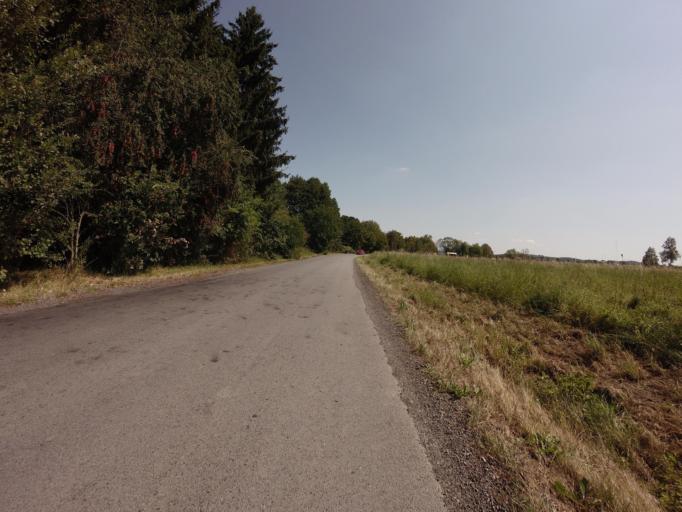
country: CZ
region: Jihocesky
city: Vcelna
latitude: 48.9338
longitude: 14.4589
